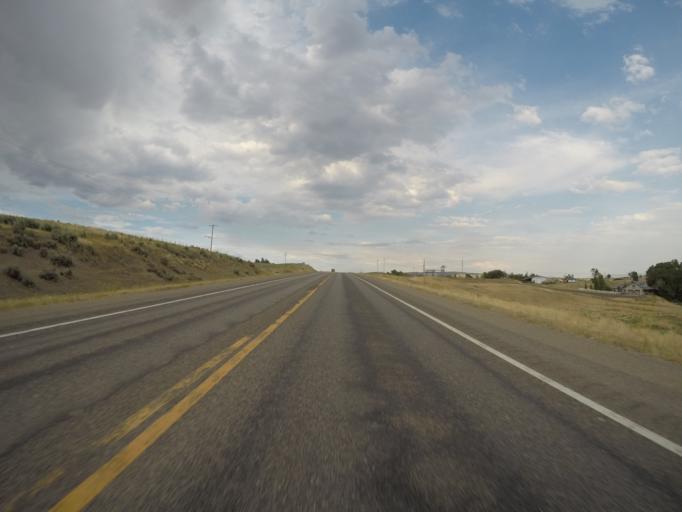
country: US
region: Colorado
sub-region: Moffat County
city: Craig
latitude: 40.5310
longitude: -107.4527
